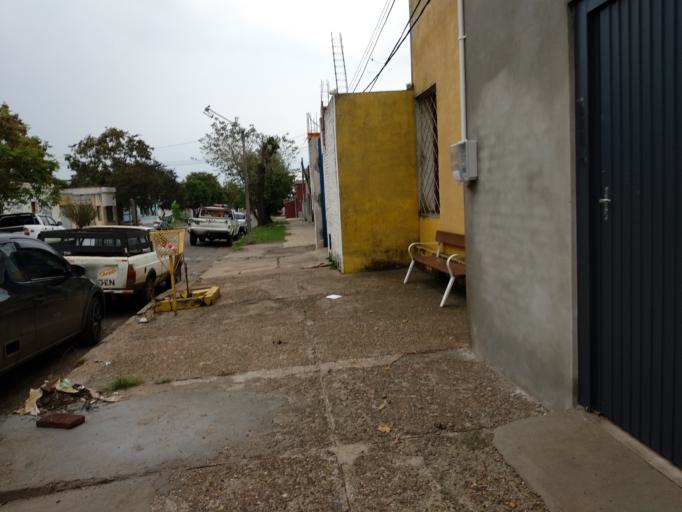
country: UY
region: Artigas
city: Artigas
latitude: -30.4010
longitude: -56.4691
